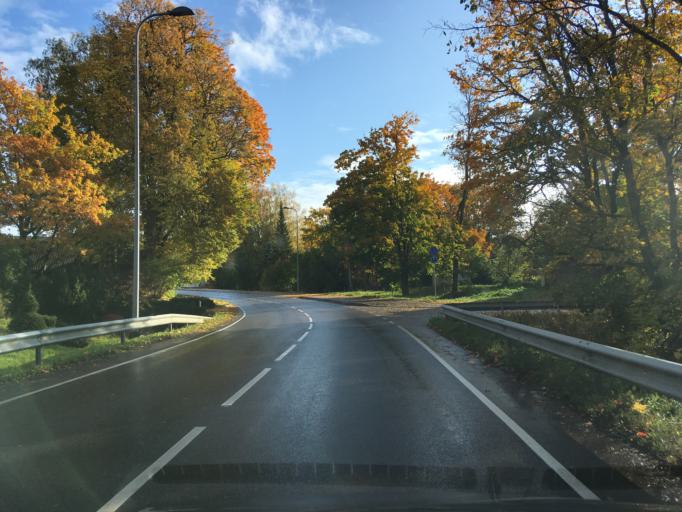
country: EE
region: Harju
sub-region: Raasiku vald
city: Raasiku
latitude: 59.1864
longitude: 25.1675
